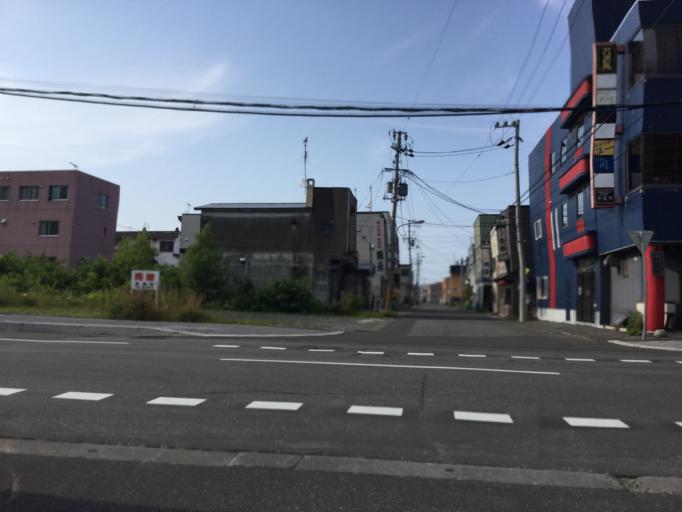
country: JP
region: Hokkaido
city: Wakkanai
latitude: 45.4192
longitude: 141.6742
